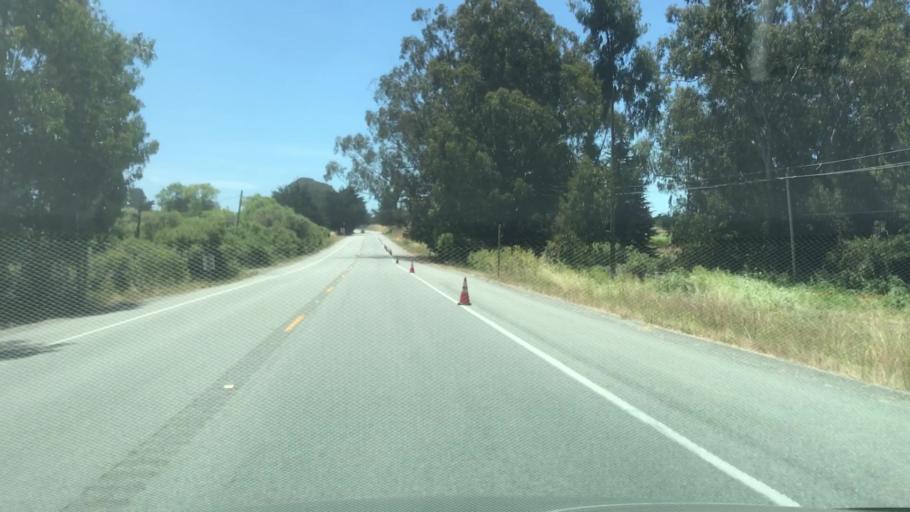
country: US
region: California
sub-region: San Mateo County
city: Half Moon Bay
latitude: 37.4283
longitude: -122.4265
